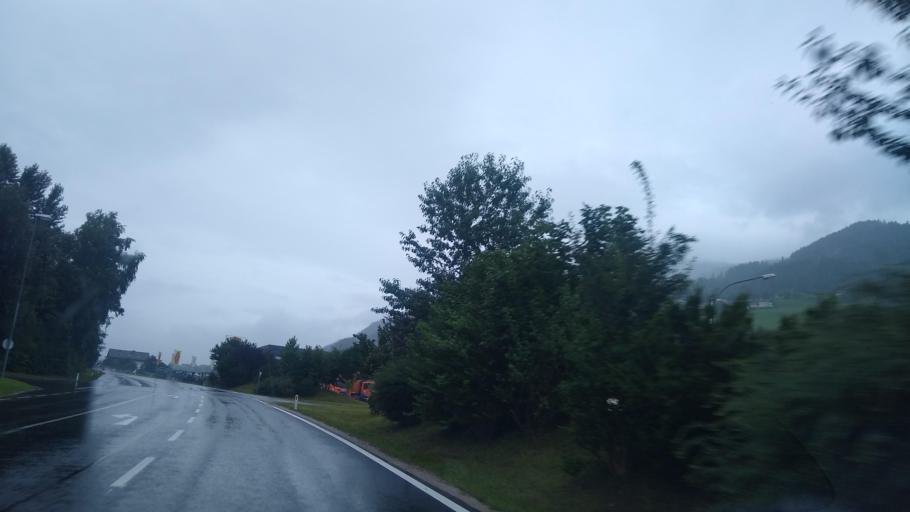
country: AT
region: Tyrol
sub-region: Politischer Bezirk Schwaz
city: Stans
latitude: 47.3628
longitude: 11.7277
